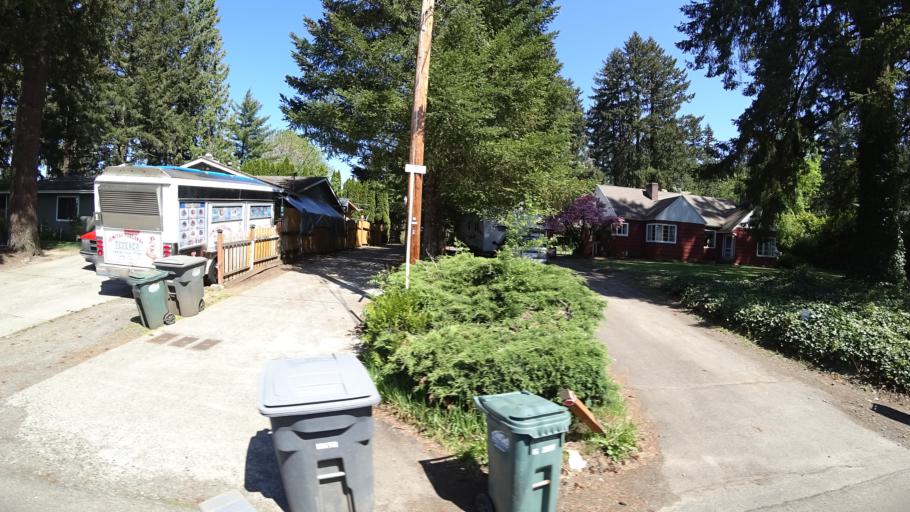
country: US
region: Oregon
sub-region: Washington County
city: Hillsboro
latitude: 45.5199
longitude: -122.9581
